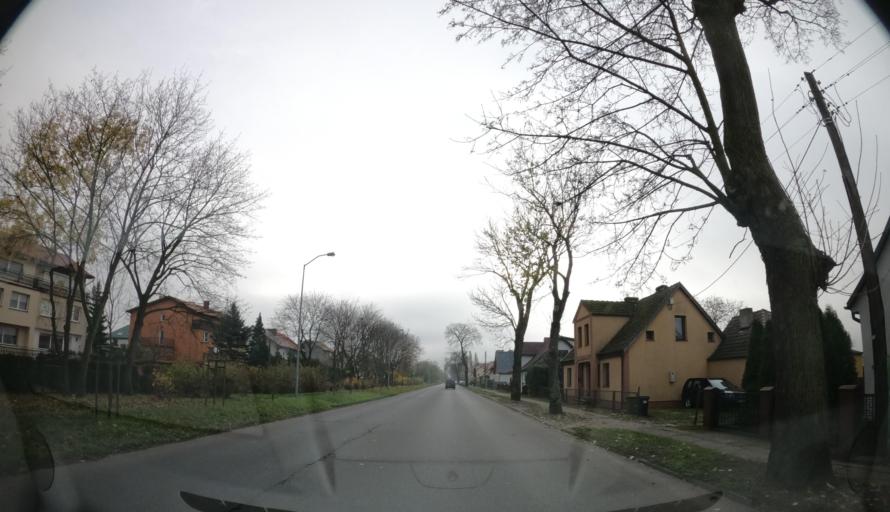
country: PL
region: West Pomeranian Voivodeship
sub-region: Powiat goleniowski
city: Goleniow
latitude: 53.5742
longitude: 14.8305
